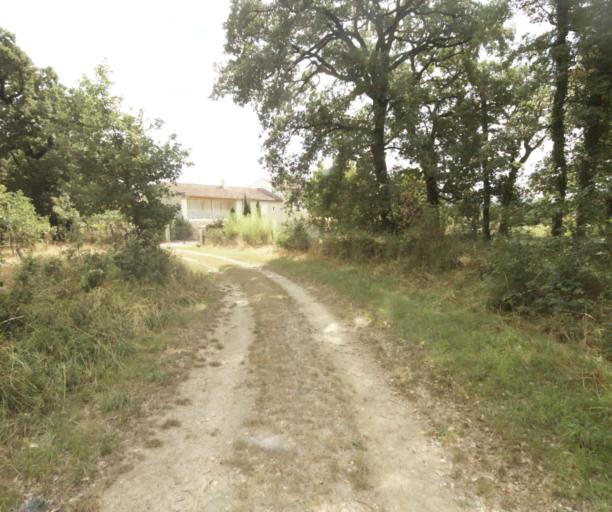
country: FR
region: Midi-Pyrenees
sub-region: Departement de la Haute-Garonne
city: Saint-Felix-Lauragais
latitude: 43.4375
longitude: 1.9273
